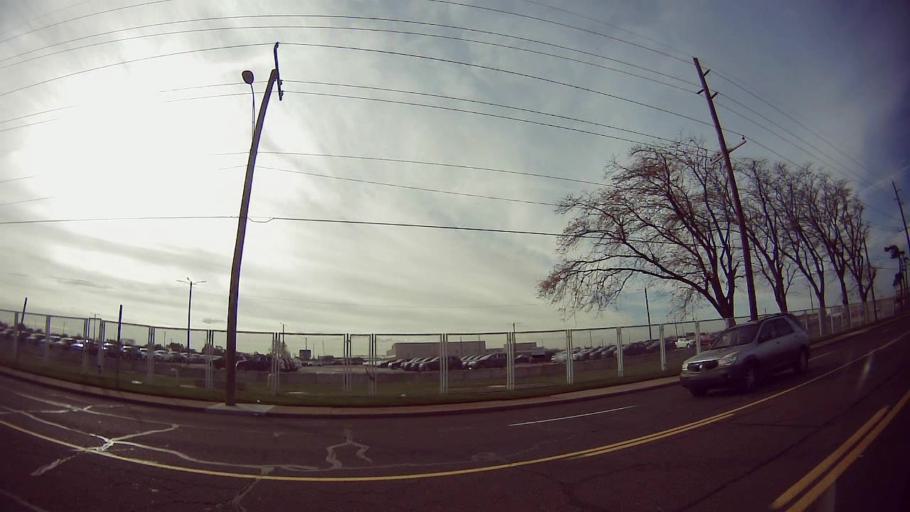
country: US
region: Michigan
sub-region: Wayne County
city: Hamtramck
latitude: 42.4050
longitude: -83.0286
